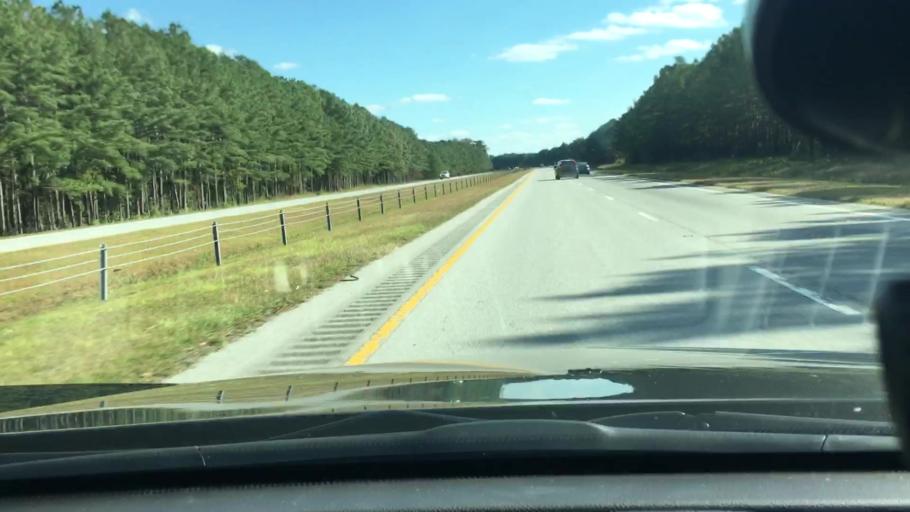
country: US
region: North Carolina
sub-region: Pitt County
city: Farmville
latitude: 35.6320
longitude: -77.7192
